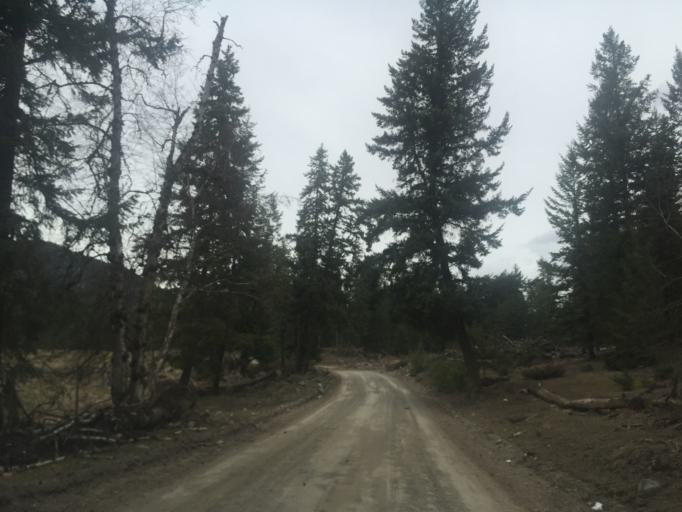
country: CA
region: British Columbia
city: Kamloops
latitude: 51.3645
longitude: -120.1541
